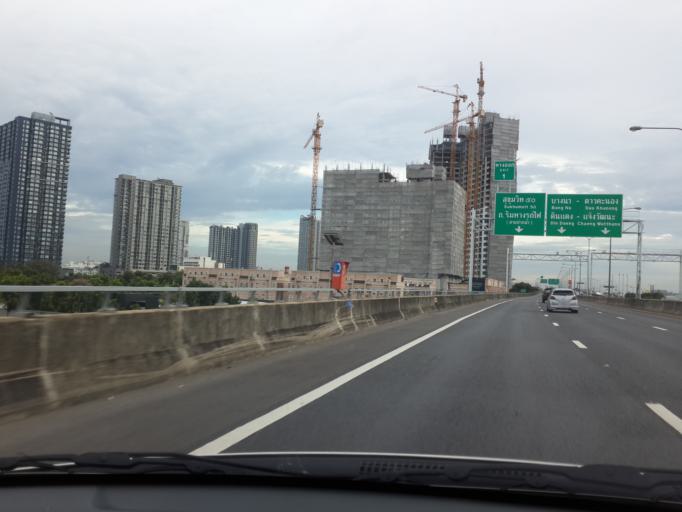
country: TH
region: Bangkok
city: Phra Khanong
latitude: 13.7158
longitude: 100.6013
